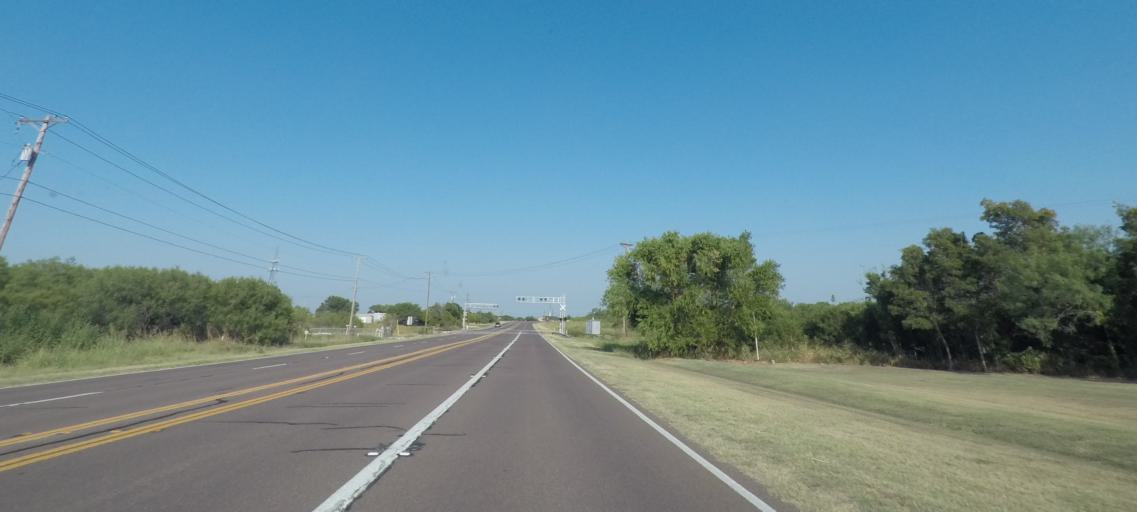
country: US
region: Texas
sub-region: Archer County
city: Holliday
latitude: 33.8592
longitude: -98.5938
